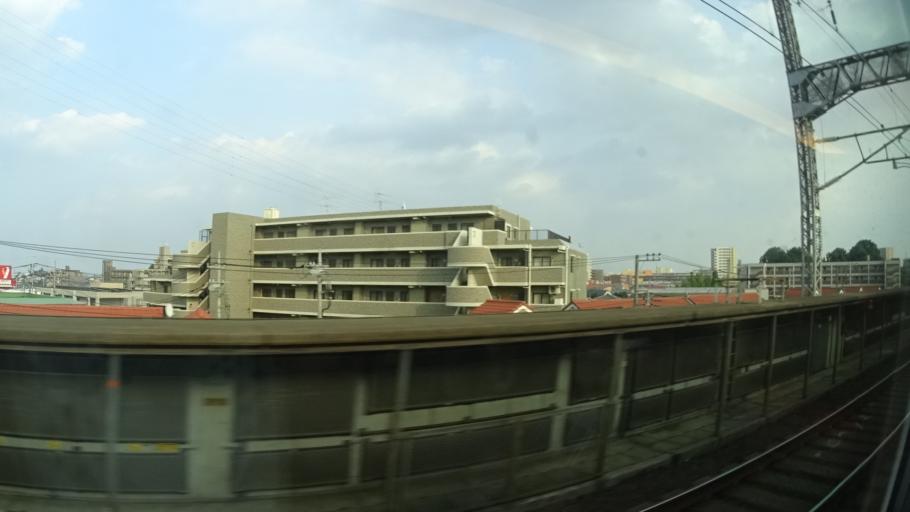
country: JP
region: Saitama
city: Ageoshimo
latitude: 35.9398
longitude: 139.6177
